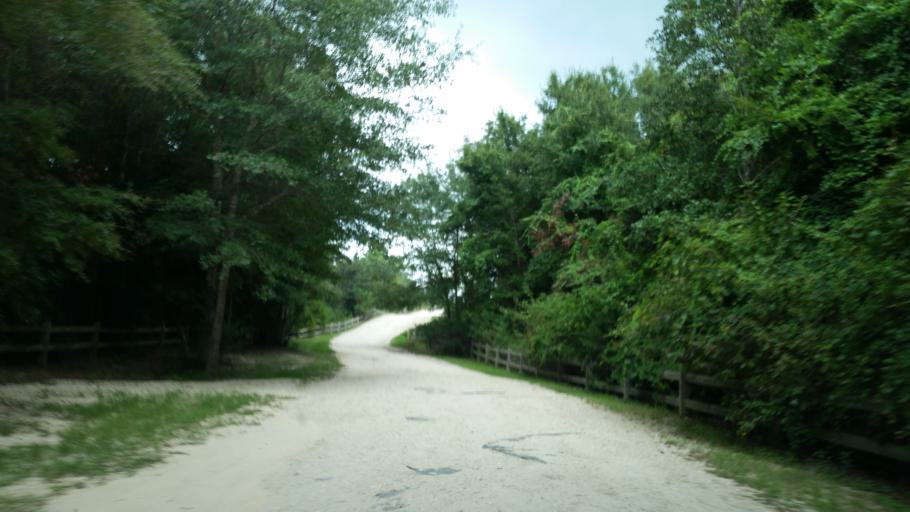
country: US
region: Florida
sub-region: Escambia County
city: Cantonment
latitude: 30.6755
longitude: -87.4055
